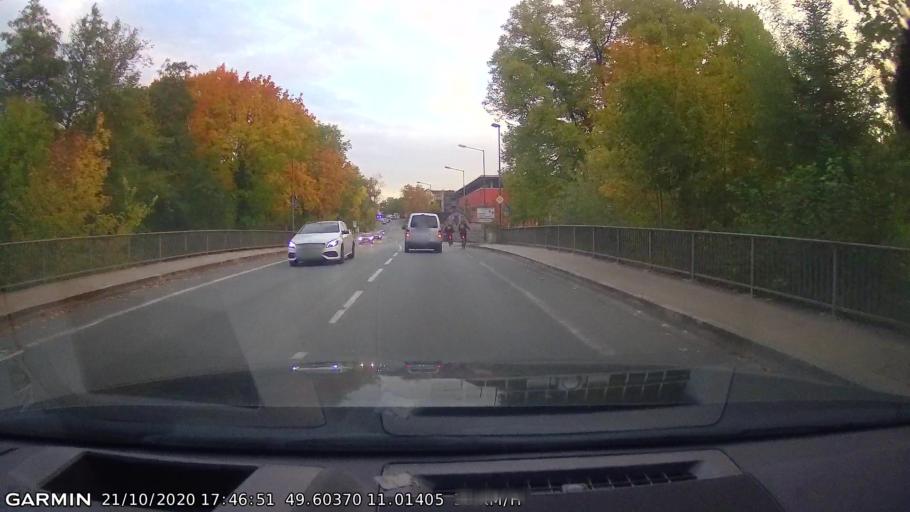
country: DE
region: Bavaria
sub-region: Regierungsbezirk Mittelfranken
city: Erlangen
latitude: 49.6035
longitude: 11.0141
